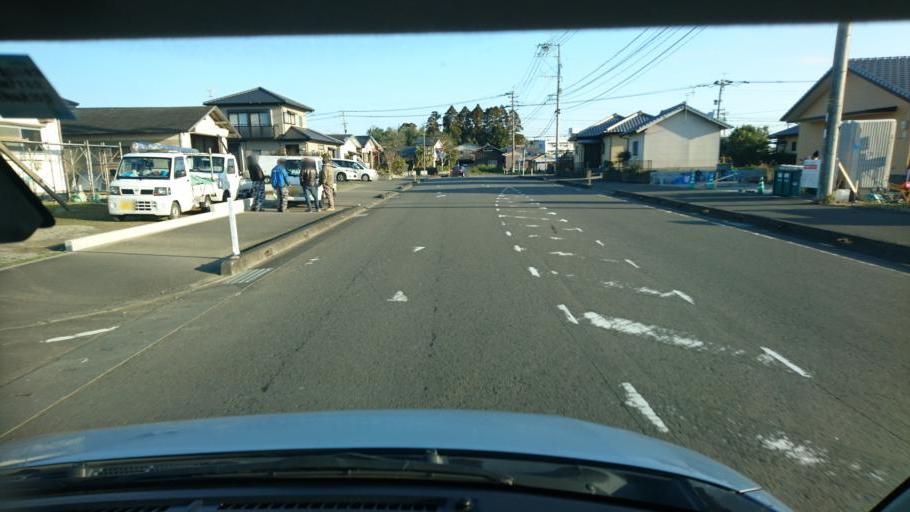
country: JP
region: Miyazaki
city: Miyazaki-shi
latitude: 31.8395
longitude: 131.4202
